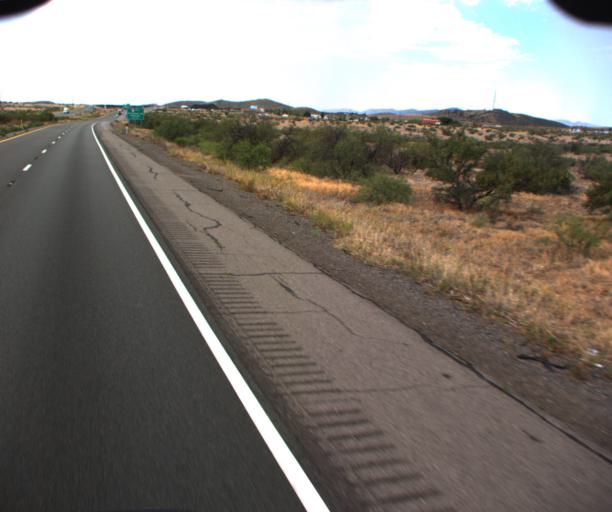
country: US
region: Arizona
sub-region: Yavapai County
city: Cordes Lakes
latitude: 34.3449
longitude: -112.1178
